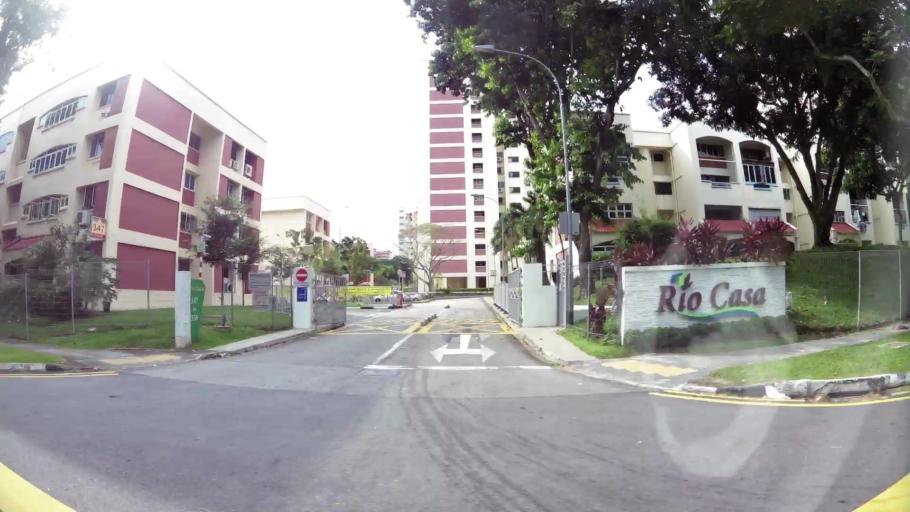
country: SG
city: Singapore
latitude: 1.3713
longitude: 103.9008
